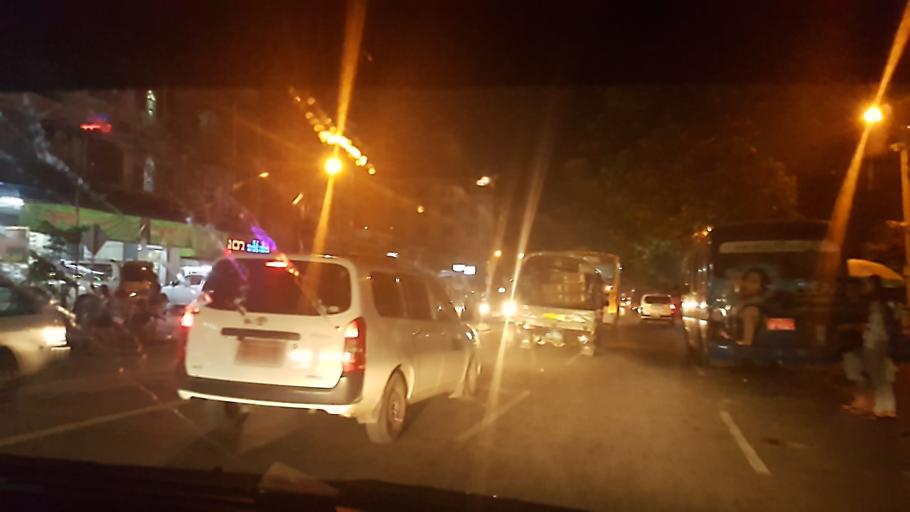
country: MM
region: Yangon
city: Yangon
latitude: 16.8094
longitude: 96.1261
